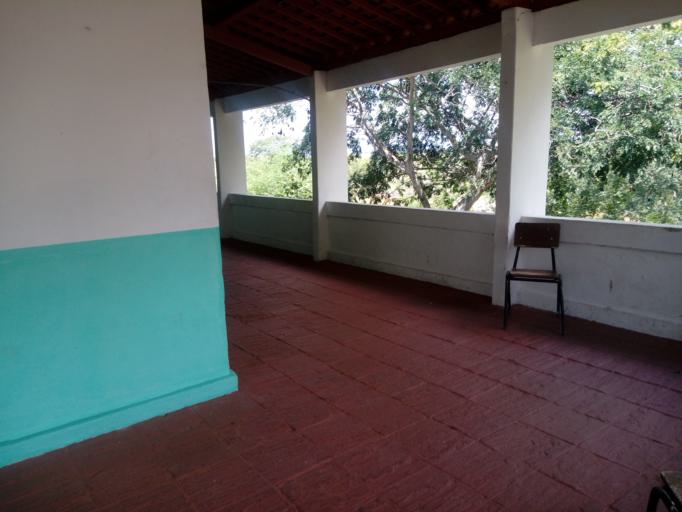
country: BR
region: Paraiba
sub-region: Inga
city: Inga
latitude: -7.3246
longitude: -35.5850
